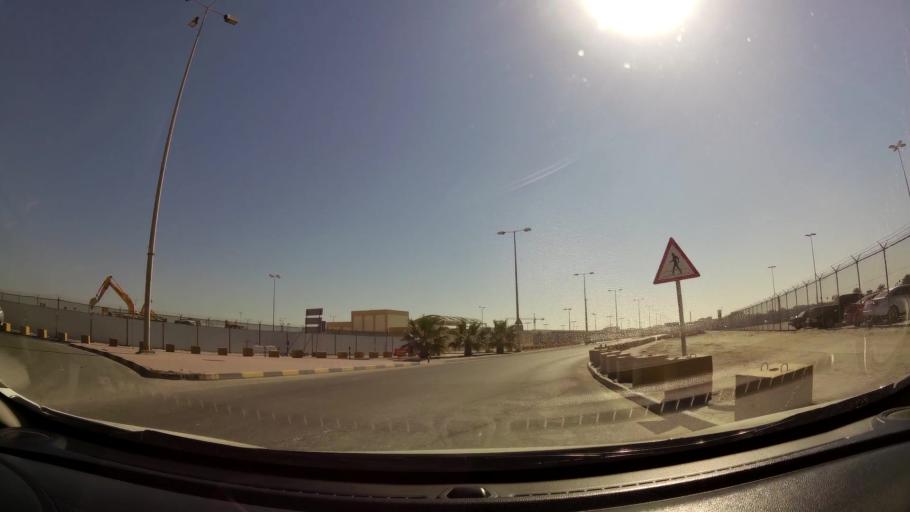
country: BH
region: Muharraq
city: Al Muharraq
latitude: 26.2646
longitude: 50.6298
